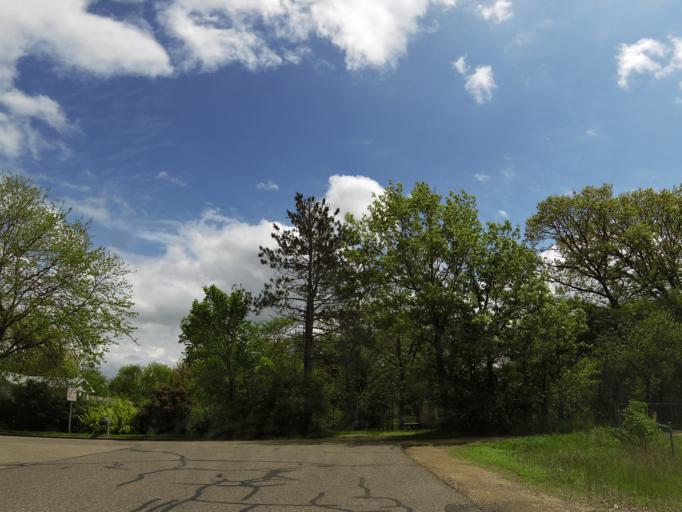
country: US
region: Wisconsin
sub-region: Saint Croix County
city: Hudson
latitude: 44.9813
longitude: -92.7367
